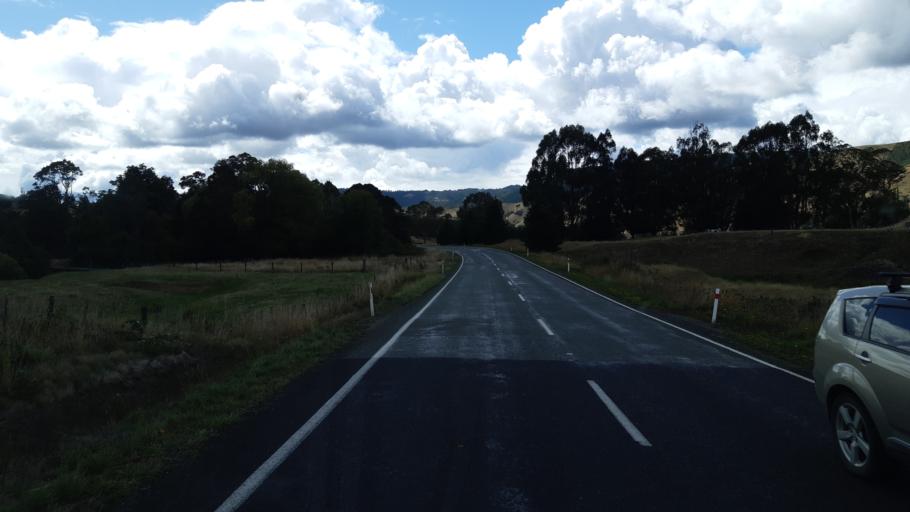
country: NZ
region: Tasman
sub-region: Tasman District
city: Wakefield
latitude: -41.5621
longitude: 172.7797
